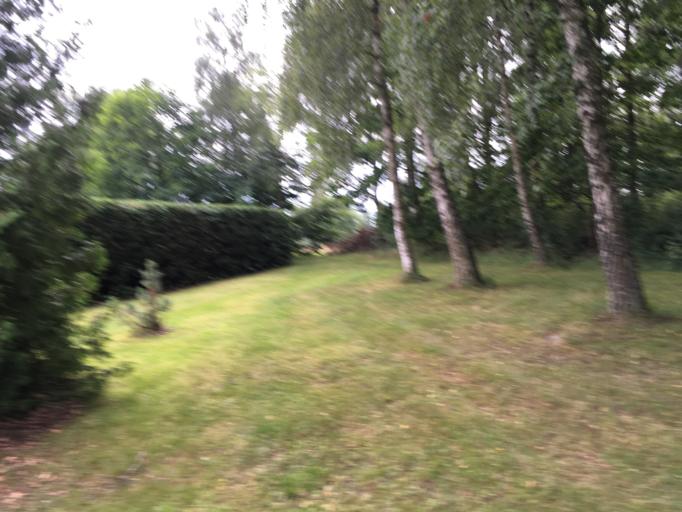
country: SE
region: Halland
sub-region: Laholms Kommun
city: Veinge
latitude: 56.5508
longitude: 13.0688
